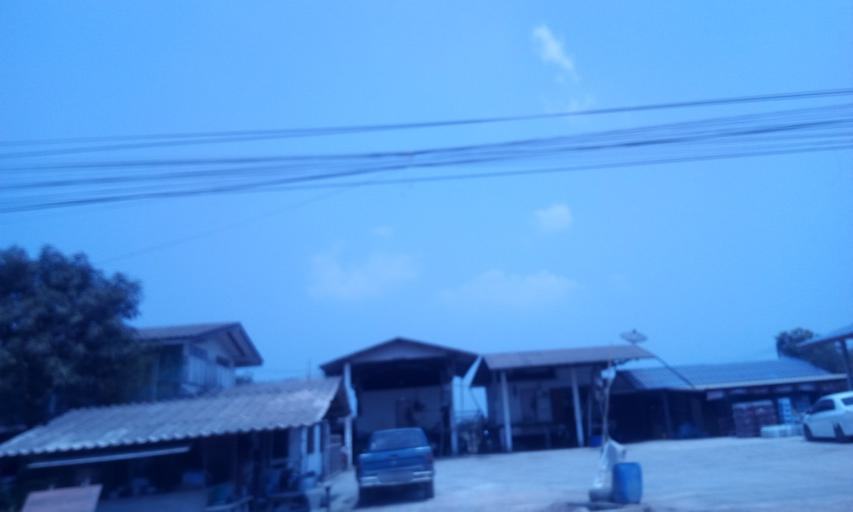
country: TH
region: Chachoengsao
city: Ban Pho
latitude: 13.5908
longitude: 101.1213
